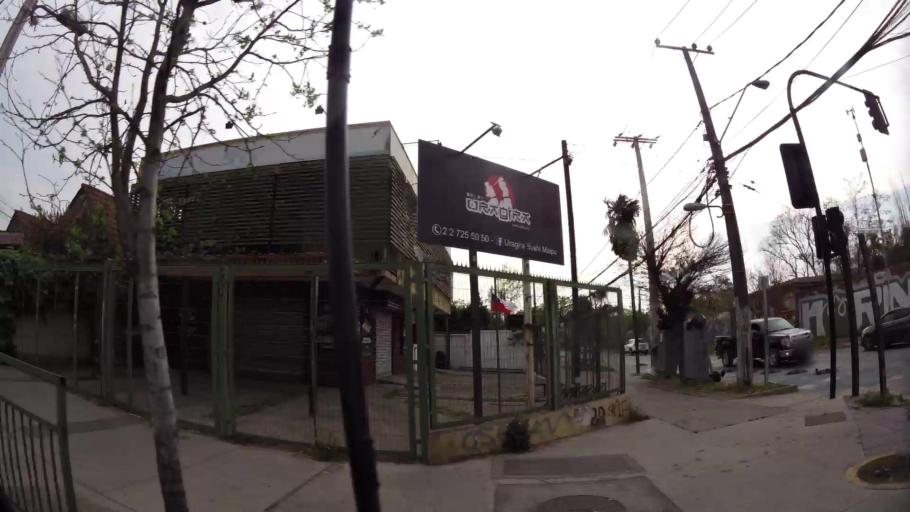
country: CL
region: Santiago Metropolitan
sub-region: Provincia de Santiago
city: Lo Prado
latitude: -33.5210
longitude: -70.7574
